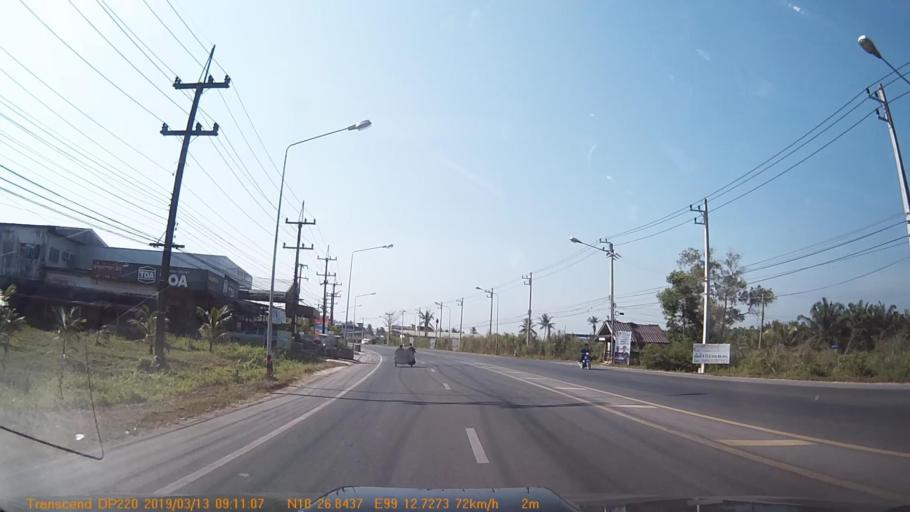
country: TH
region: Chumphon
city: Chumphon
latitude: 10.4472
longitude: 99.2121
